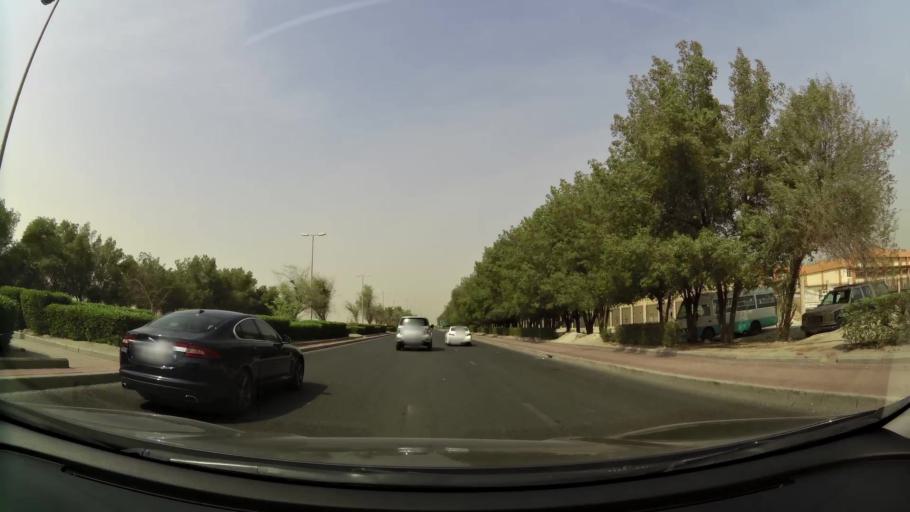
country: KW
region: Al Asimah
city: Ar Rabiyah
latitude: 29.2581
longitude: 47.9161
